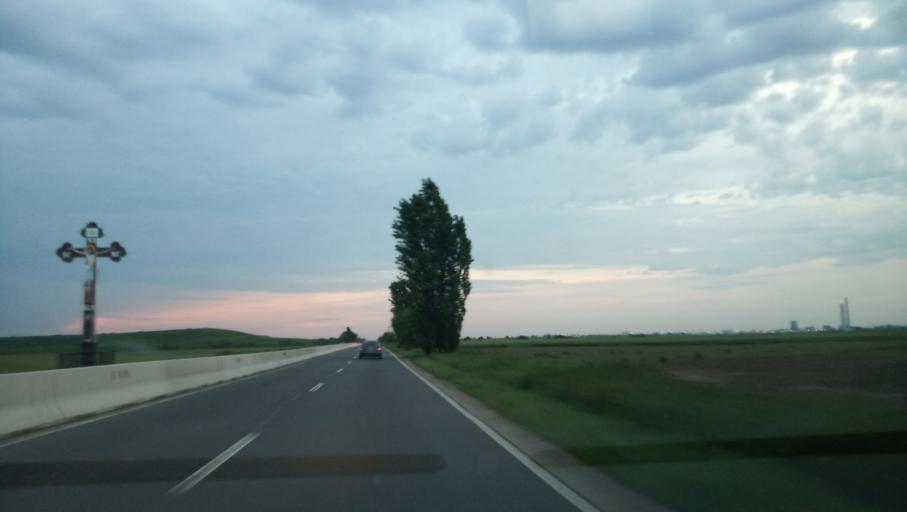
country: RO
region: Timis
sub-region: Comuna Sag
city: Sag
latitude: 45.6710
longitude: 21.1714
